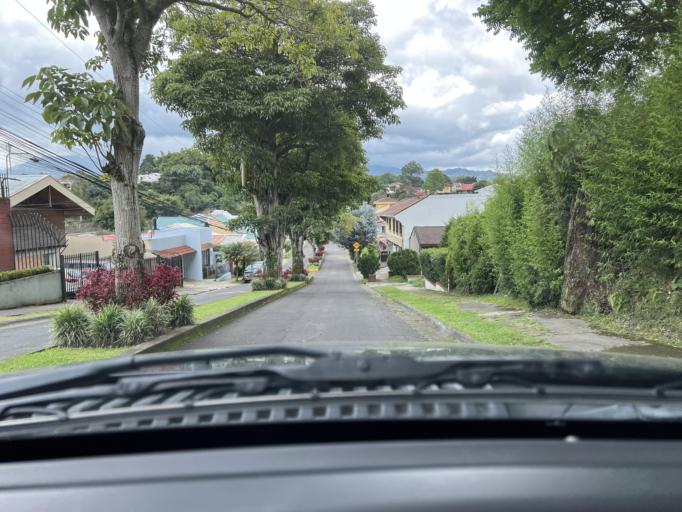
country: CR
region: San Jose
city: Granadilla
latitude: 9.9424
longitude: -84.0234
